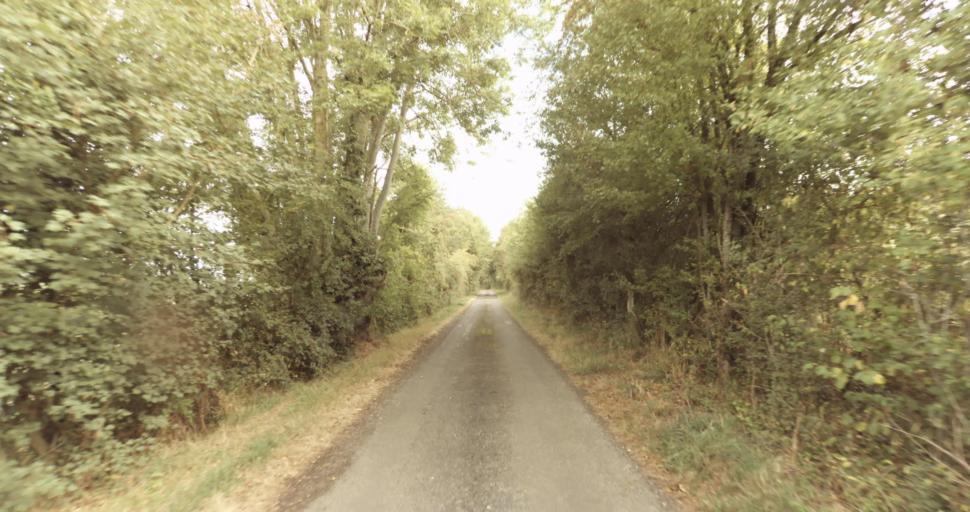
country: FR
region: Lower Normandy
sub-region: Departement de l'Orne
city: Vimoutiers
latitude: 48.9384
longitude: 0.2756
